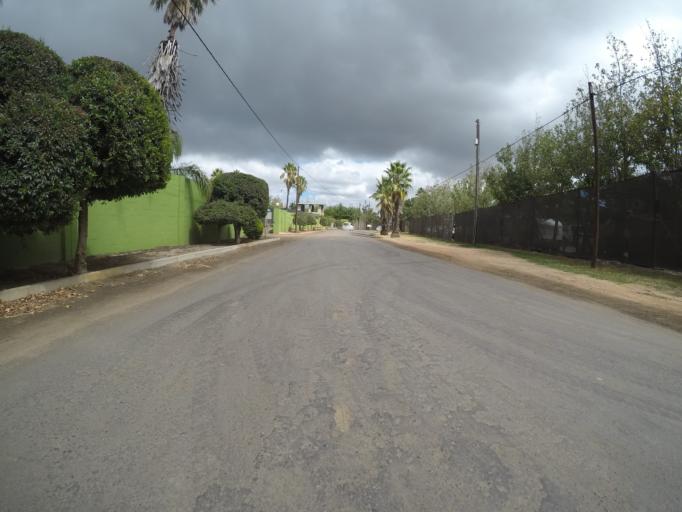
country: ZA
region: Western Cape
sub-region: City of Cape Town
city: Kraaifontein
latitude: -33.8326
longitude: 18.7379
